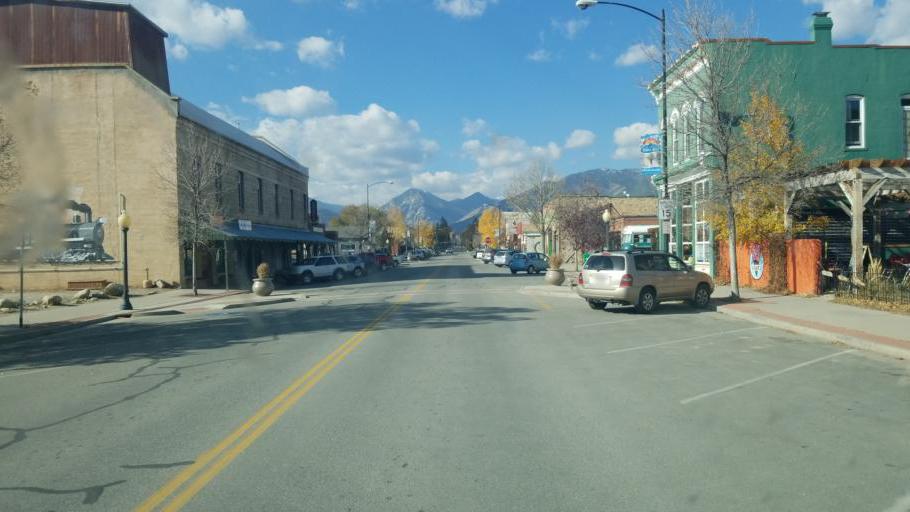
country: US
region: Colorado
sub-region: Chaffee County
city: Buena Vista
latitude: 38.8431
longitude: -106.1282
